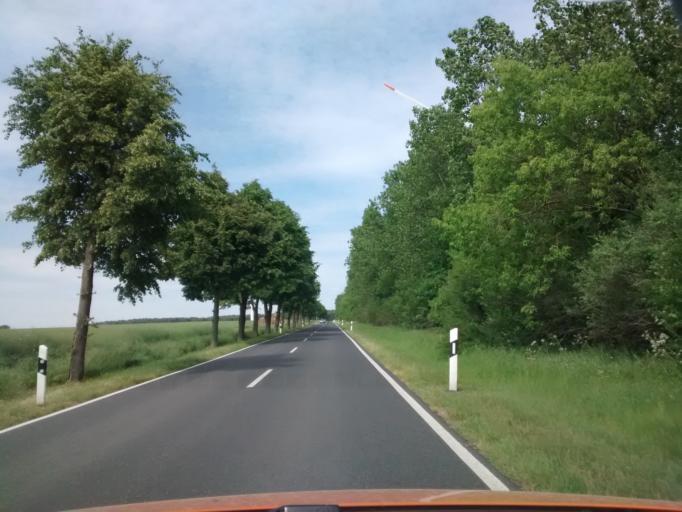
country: DE
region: Brandenburg
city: Ihlow
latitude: 51.8975
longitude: 13.3103
